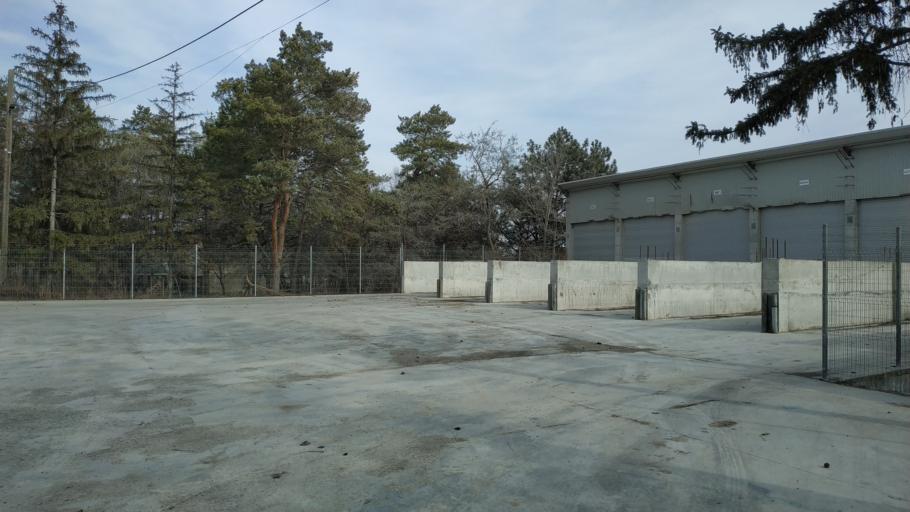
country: RO
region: Iasi
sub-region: Comuna Grozesti
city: Grozesti
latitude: 47.0417
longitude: 28.0922
